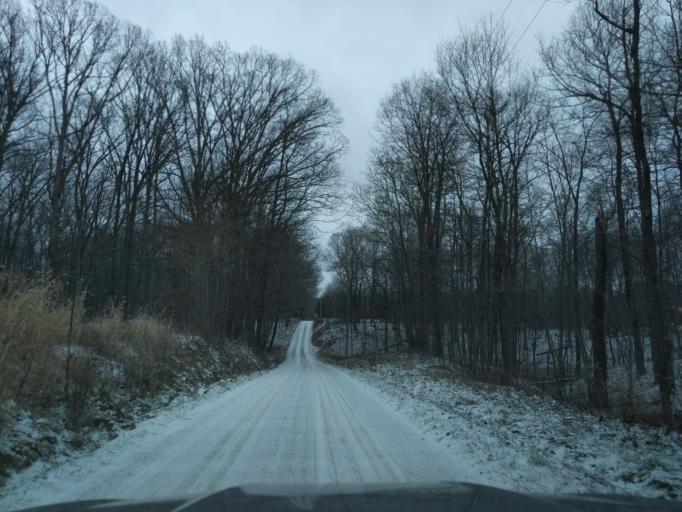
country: US
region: Indiana
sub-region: Decatur County
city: Westport
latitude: 39.2042
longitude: -85.4508
